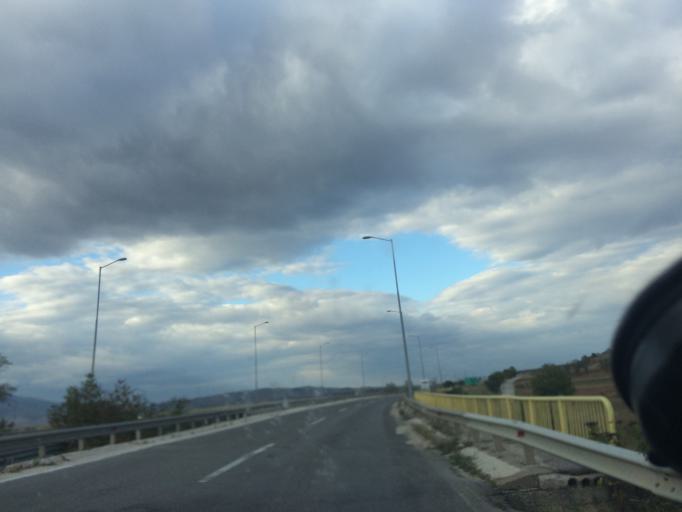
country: MK
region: Petrovec
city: Petrovec
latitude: 41.9376
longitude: 21.6266
